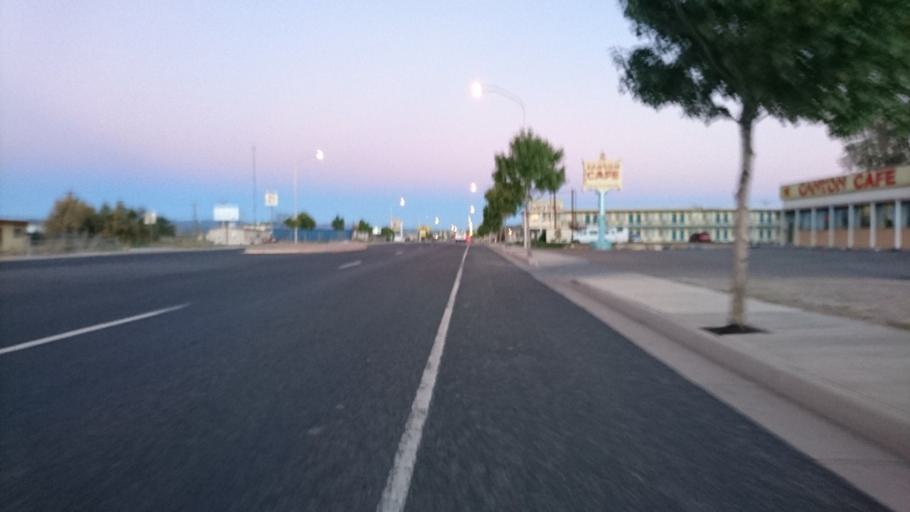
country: US
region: New Mexico
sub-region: Cibola County
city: Grants
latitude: 35.1413
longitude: -107.8316
